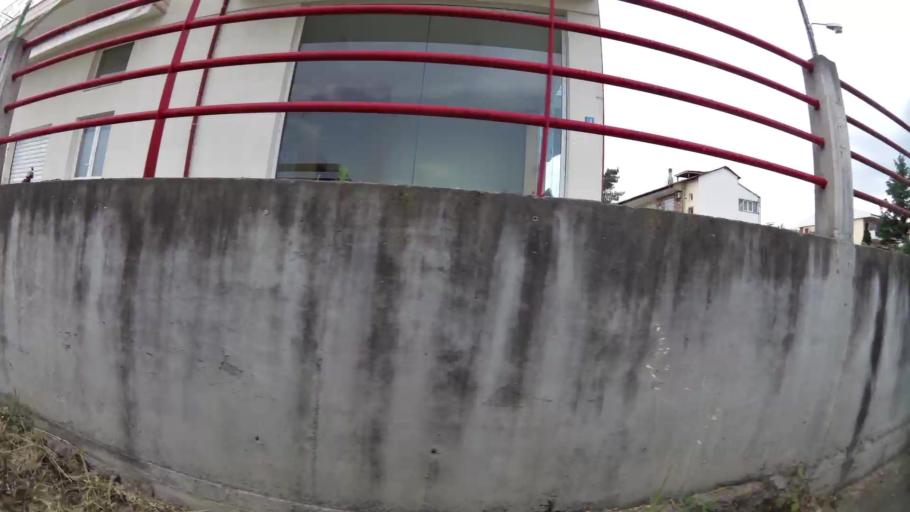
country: GR
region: Central Macedonia
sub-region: Nomos Imathias
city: Veroia
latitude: 40.5325
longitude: 22.2083
